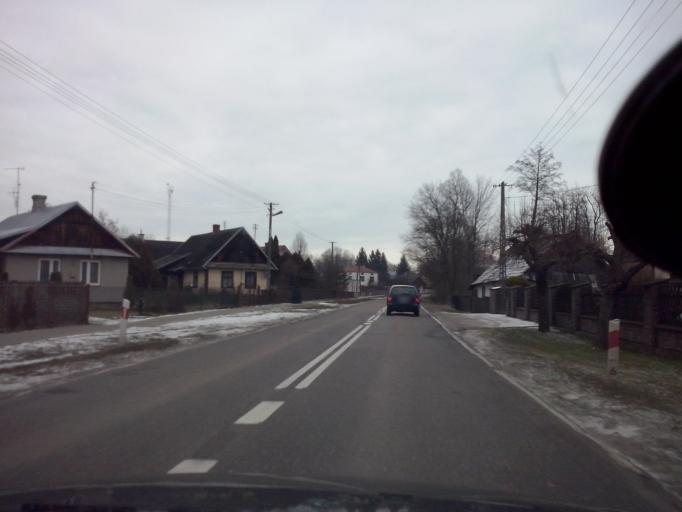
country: PL
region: Lublin Voivodeship
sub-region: Powiat bilgorajski
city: Bilgoraj
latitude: 50.5144
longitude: 22.6584
